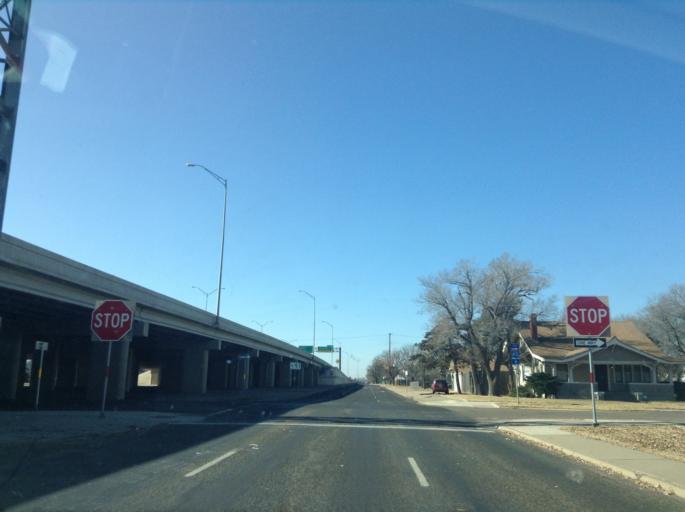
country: US
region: Texas
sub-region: Potter County
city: Amarillo
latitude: 35.1939
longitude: -101.8408
